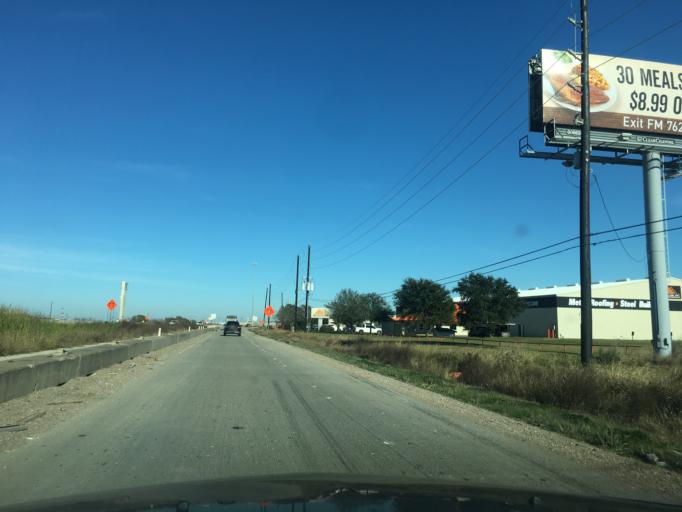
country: US
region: Texas
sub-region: Fort Bend County
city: Rosenberg
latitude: 29.5265
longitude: -95.8688
